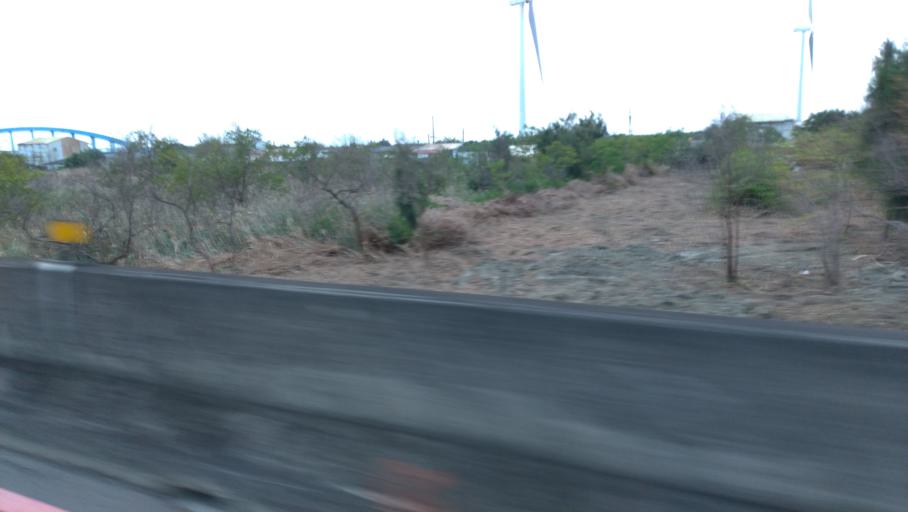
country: TW
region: Taiwan
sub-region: Hsinchu
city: Hsinchu
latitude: 24.7616
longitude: 120.9078
